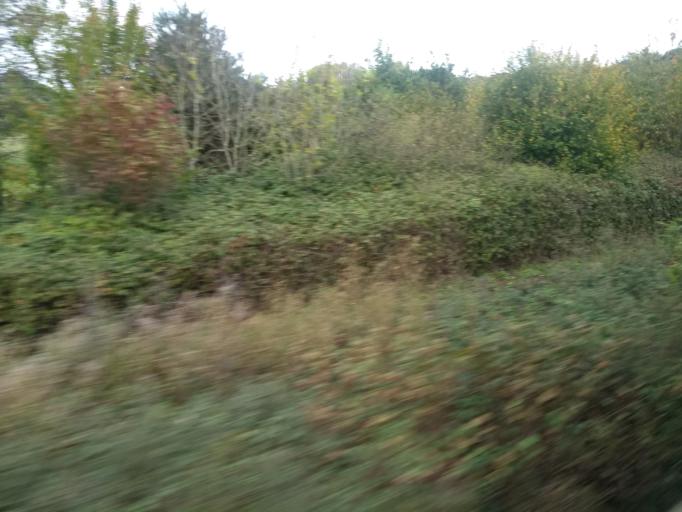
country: GB
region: England
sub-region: Isle of Wight
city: Ryde
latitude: 50.7276
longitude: -1.2006
